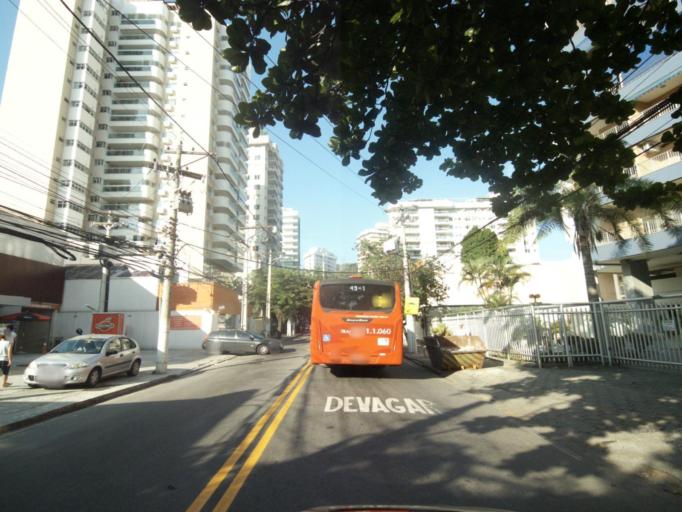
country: BR
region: Rio de Janeiro
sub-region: Niteroi
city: Niteroi
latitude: -22.8978
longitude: -43.1026
